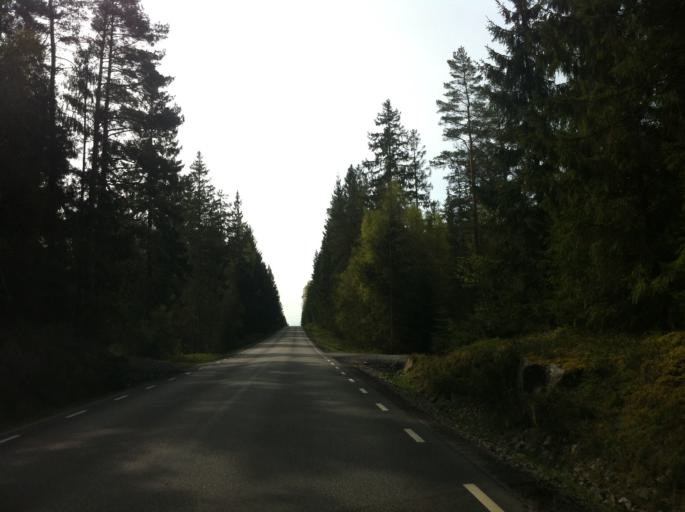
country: SE
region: Vaestra Goetaland
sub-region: Marks Kommun
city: Fritsla
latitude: 57.3894
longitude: 12.8544
